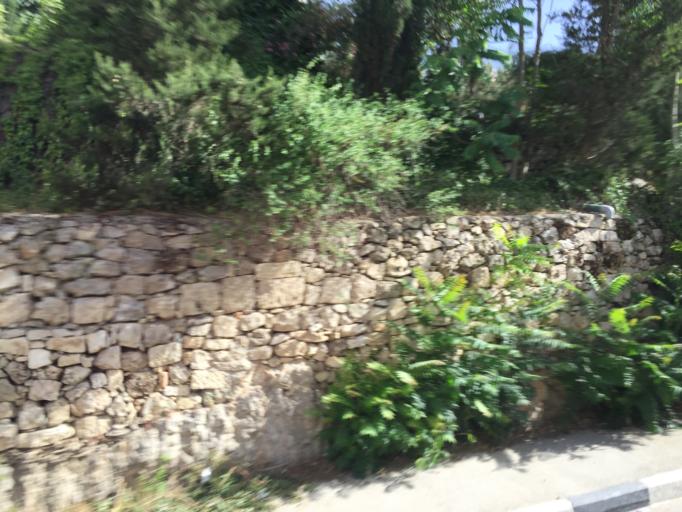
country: PS
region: West Bank
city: Bayt Jala
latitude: 31.7160
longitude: 35.1795
